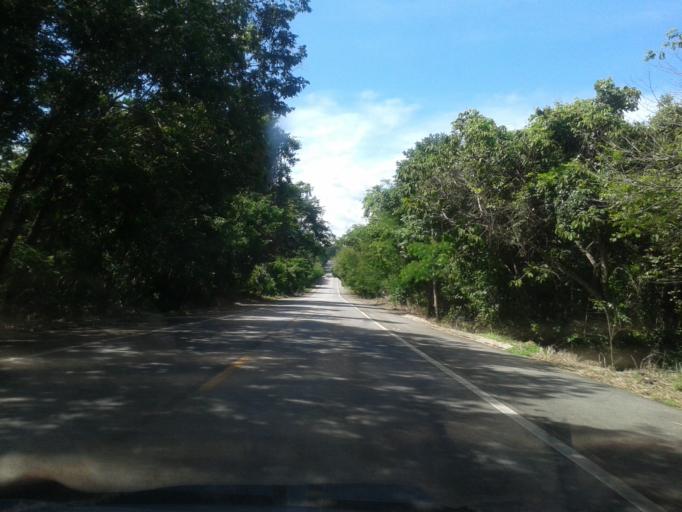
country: BR
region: Goias
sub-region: Goias
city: Goias
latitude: -15.6942
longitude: -50.1995
